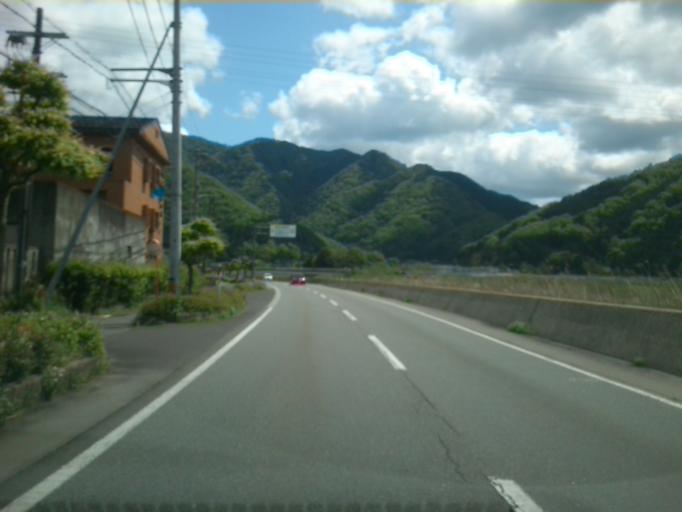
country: JP
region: Hyogo
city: Toyooka
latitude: 35.4514
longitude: 134.8719
